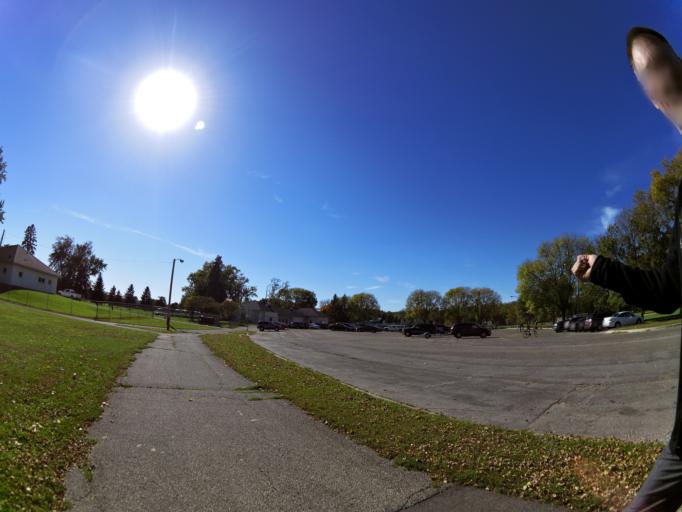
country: US
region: Minnesota
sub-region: Olmsted County
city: Rochester
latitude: 44.0671
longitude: -92.4936
